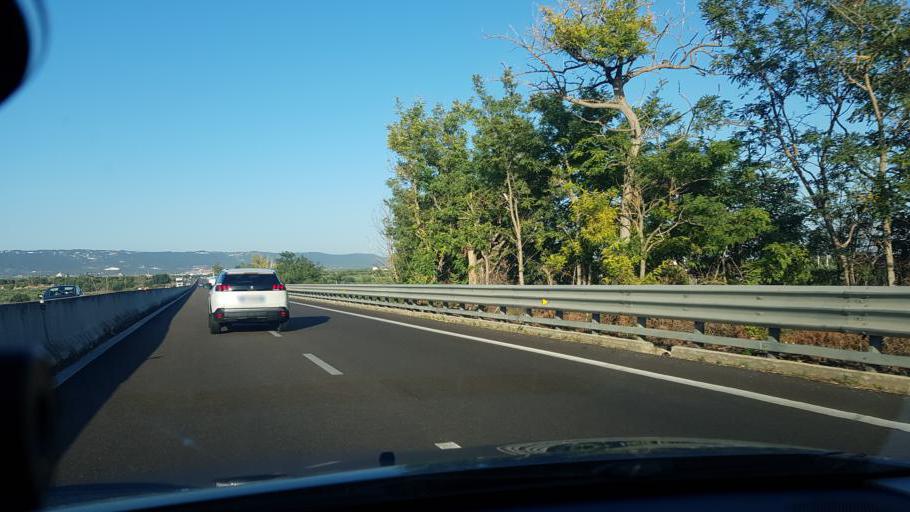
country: IT
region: Apulia
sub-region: Provincia di Brindisi
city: Pezze di Greco
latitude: 40.8336
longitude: 17.4170
